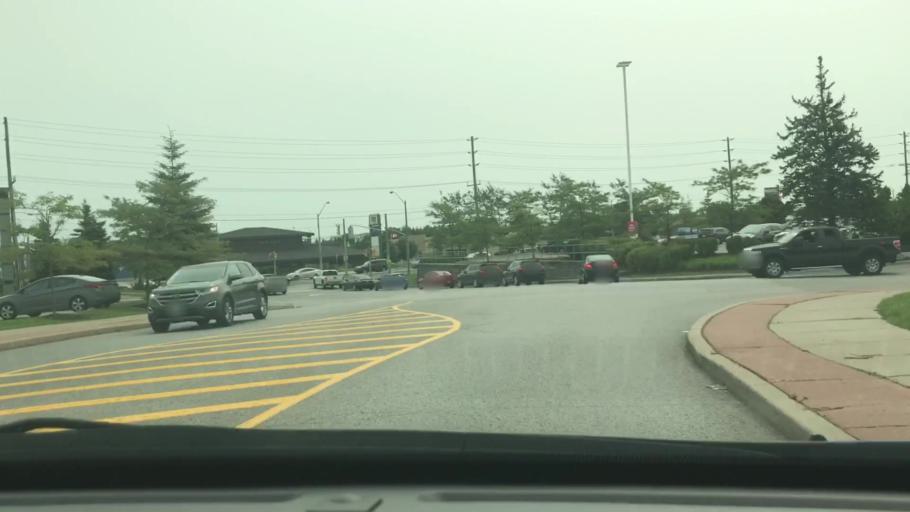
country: CA
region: Ontario
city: Newmarket
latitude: 44.0710
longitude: -79.4857
